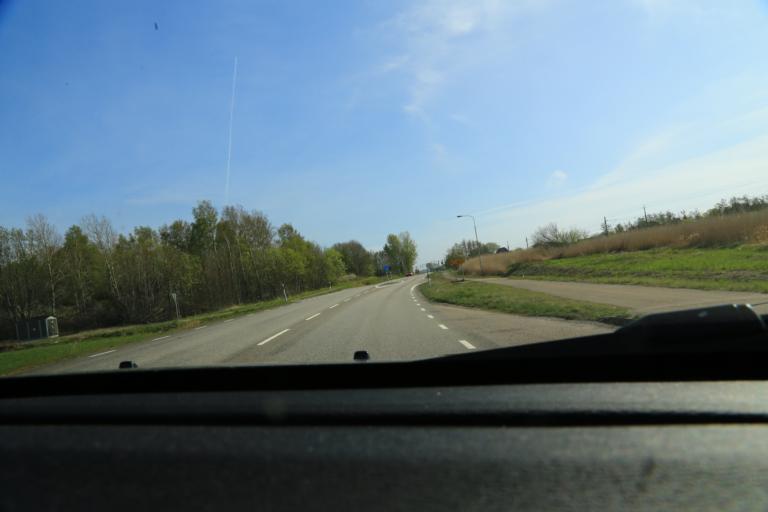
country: SE
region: Halland
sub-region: Varbergs Kommun
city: Veddige
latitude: 57.2144
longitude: 12.2222
